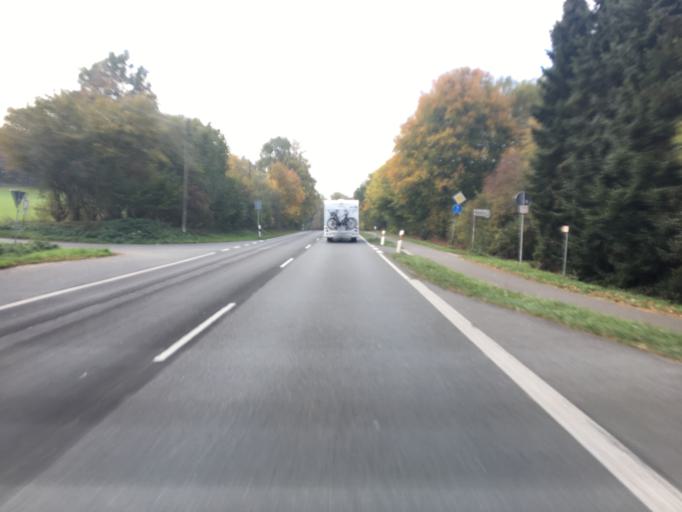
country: DE
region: North Rhine-Westphalia
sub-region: Regierungsbezirk Dusseldorf
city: Sonsbeck
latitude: 51.6278
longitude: 6.3953
